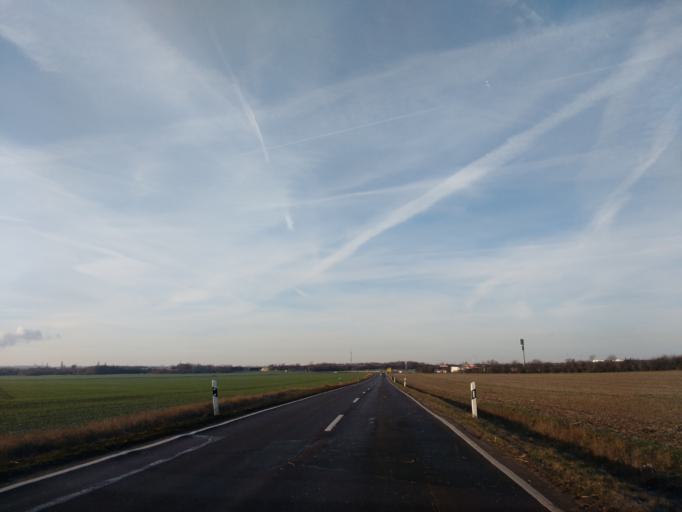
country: DE
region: Saxony-Anhalt
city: Oppin
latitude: 51.5472
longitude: 12.0212
